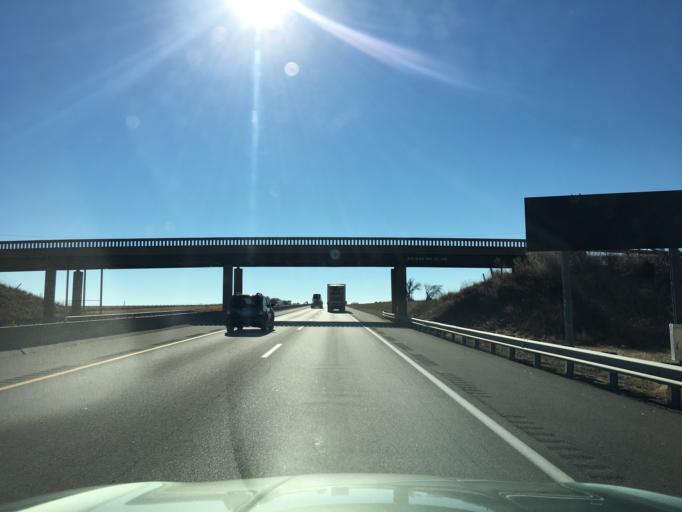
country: US
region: Kansas
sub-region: Sumner County
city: Wellington
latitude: 37.3053
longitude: -97.3405
